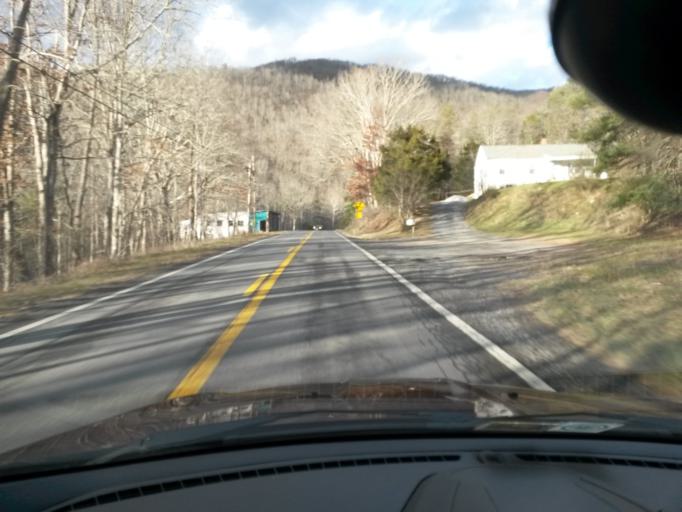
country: US
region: West Virginia
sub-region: Monroe County
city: Union
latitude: 37.5228
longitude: -80.6170
